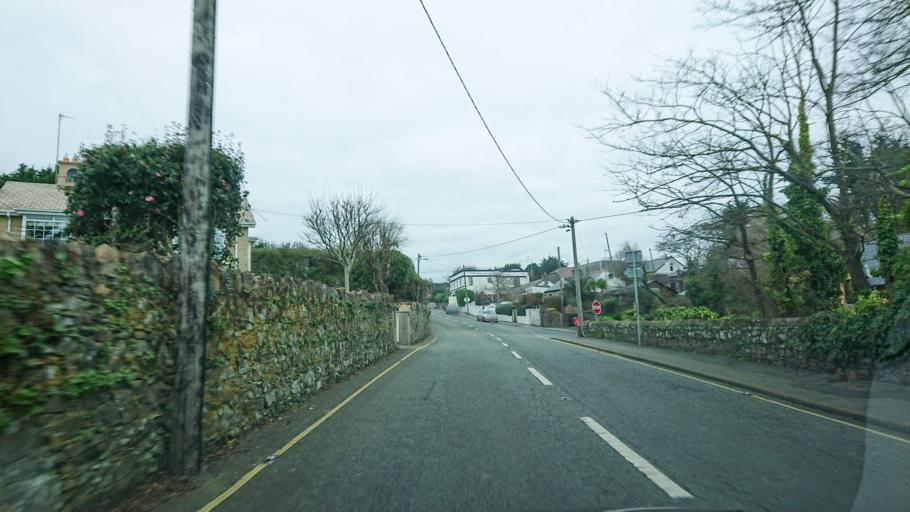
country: IE
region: Munster
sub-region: Waterford
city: Tra Mhor
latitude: 52.1551
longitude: -7.1621
